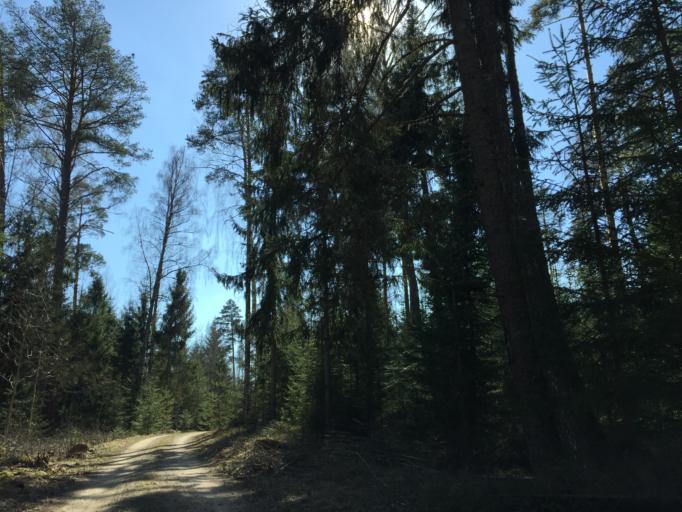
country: EE
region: Viljandimaa
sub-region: Viljandi linn
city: Viljandi
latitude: 58.2711
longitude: 25.6033
